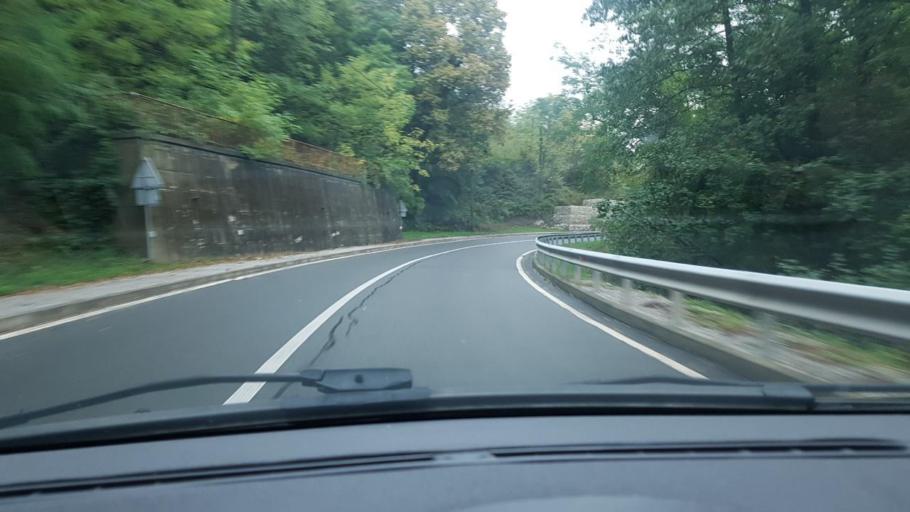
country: HR
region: Krapinsko-Zagorska
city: Marija Bistrica
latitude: 45.9792
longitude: 16.1043
